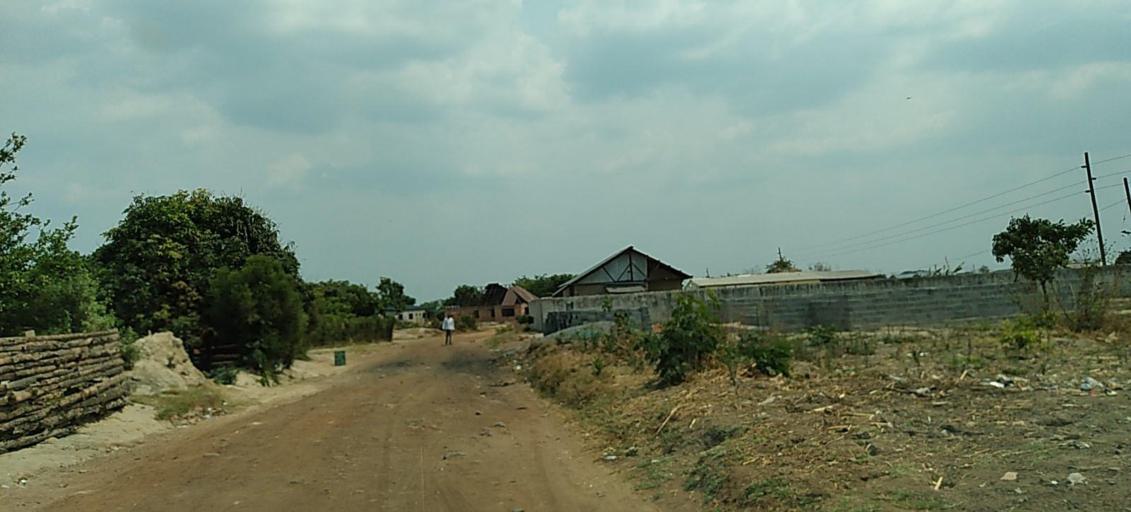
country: ZM
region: Copperbelt
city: Kalulushi
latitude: -12.8561
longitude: 28.0785
